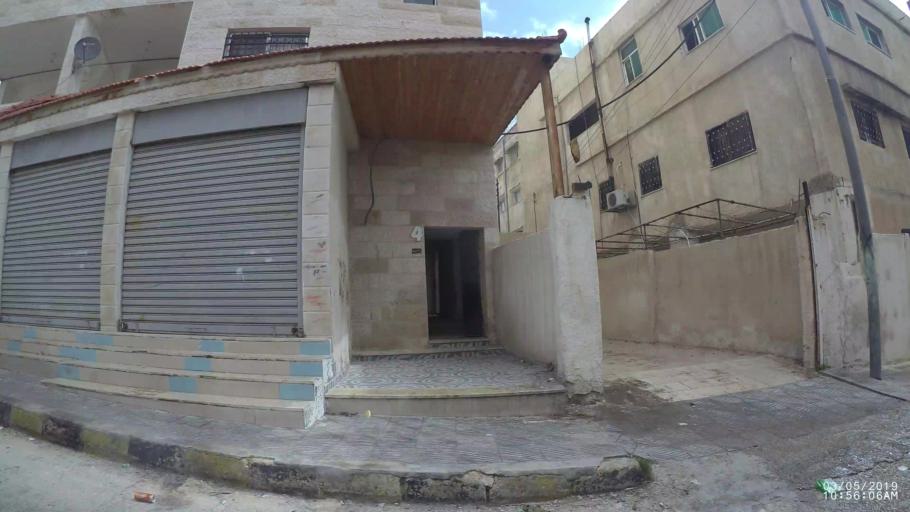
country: JO
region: Amman
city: Amman
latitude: 31.9853
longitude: 35.9217
